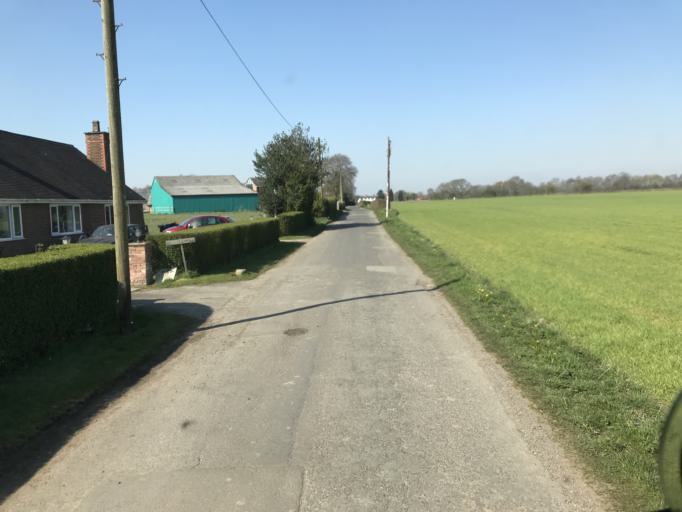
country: GB
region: England
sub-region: Trafford
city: Partington
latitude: 53.4226
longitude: -2.4698
